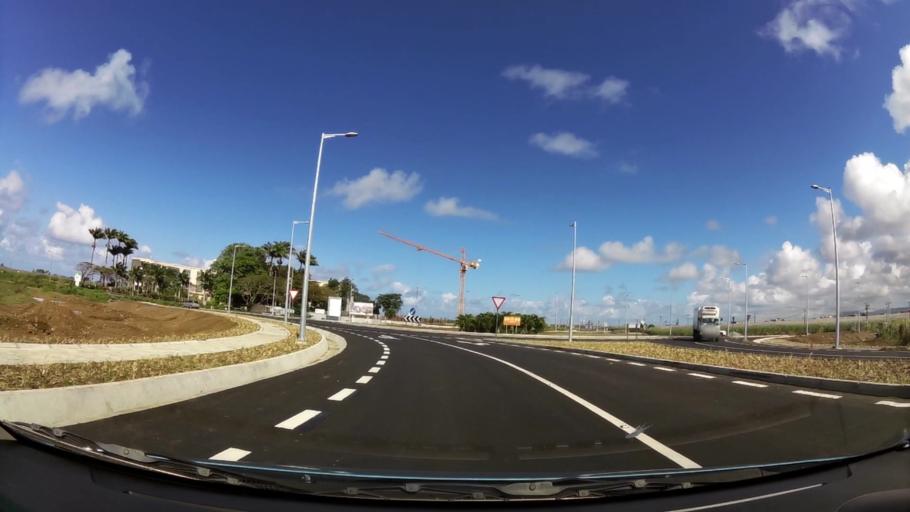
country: MU
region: Grand Port
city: Plaine Magnien
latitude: -20.4386
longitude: 57.6715
